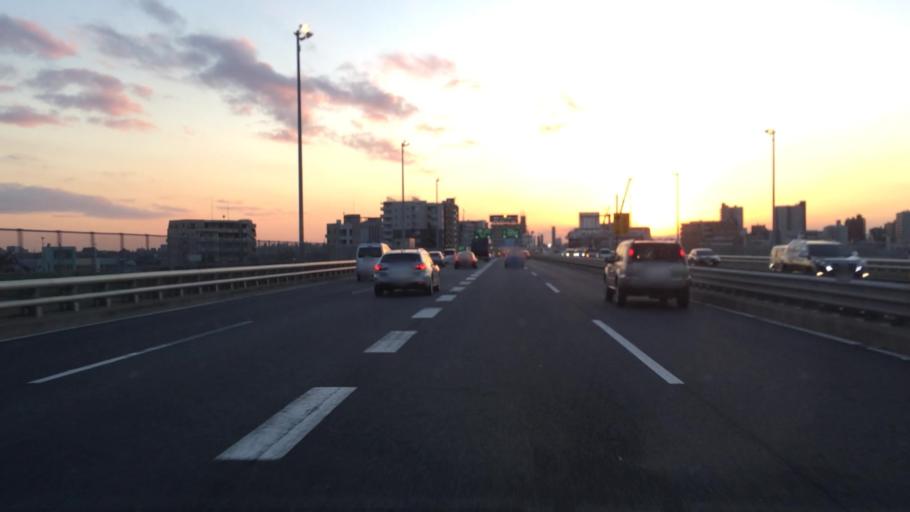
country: JP
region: Tokyo
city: Urayasu
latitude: 35.7083
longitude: 139.9144
